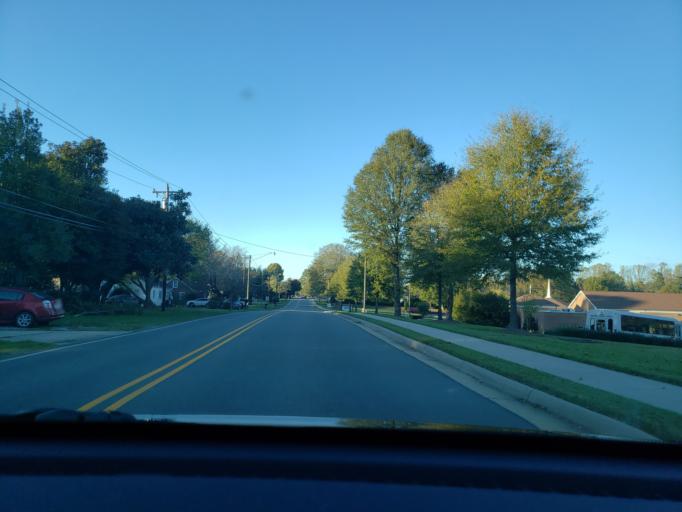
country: US
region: North Carolina
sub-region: Forsyth County
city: Walkertown
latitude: 36.1619
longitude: -80.1463
